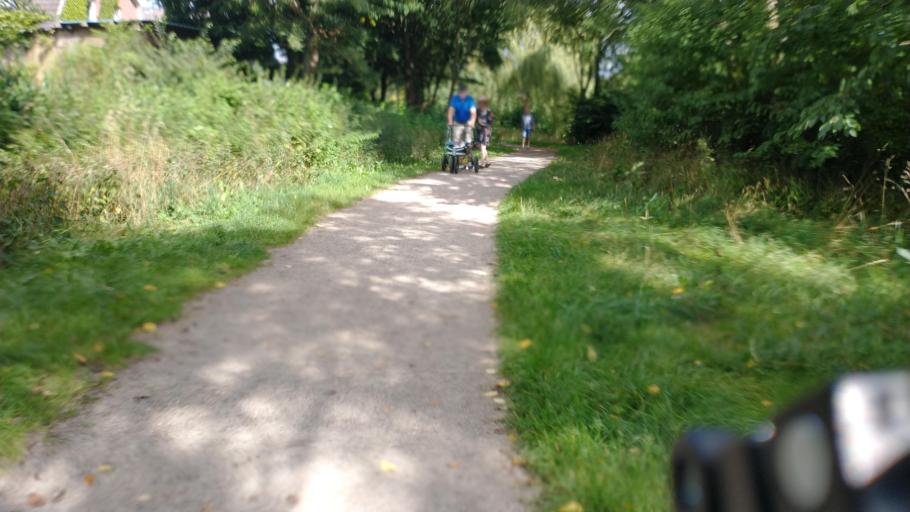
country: DE
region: Schleswig-Holstein
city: Bad Oldesloe
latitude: 53.8045
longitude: 10.3575
